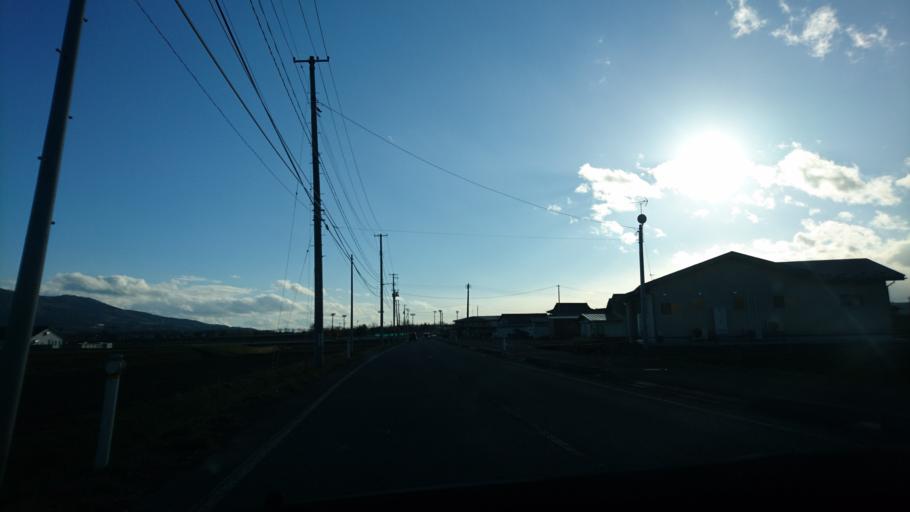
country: JP
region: Iwate
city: Mizusawa
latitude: 39.0618
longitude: 141.1435
